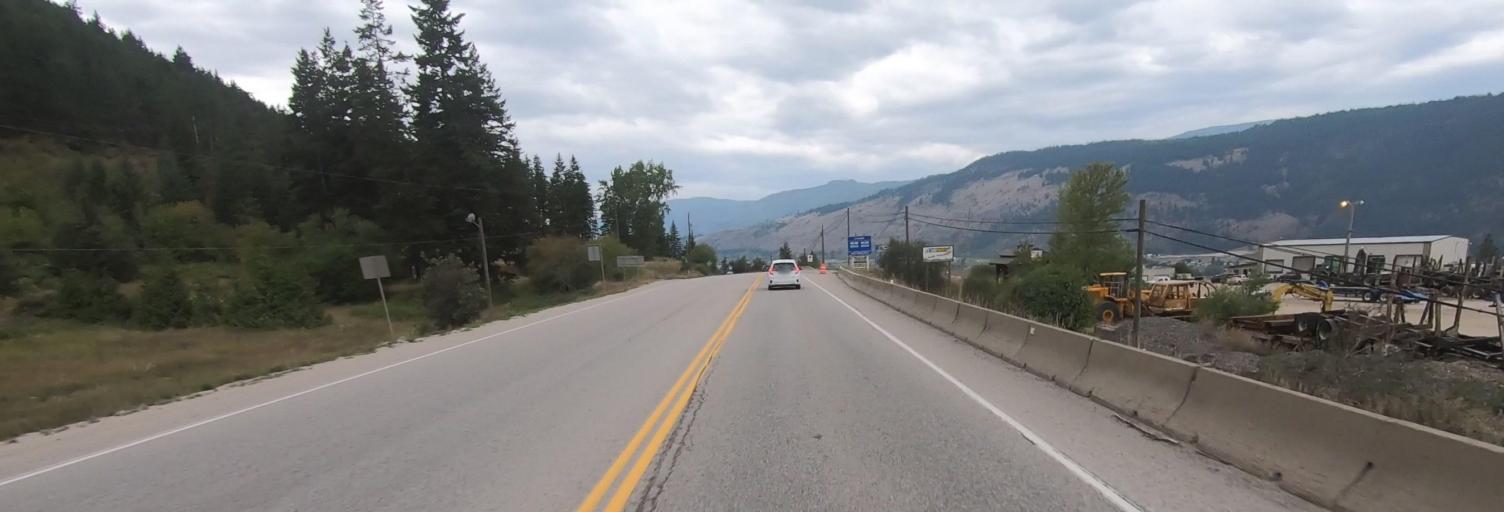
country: CA
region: British Columbia
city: Chase
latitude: 50.8278
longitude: -119.6670
